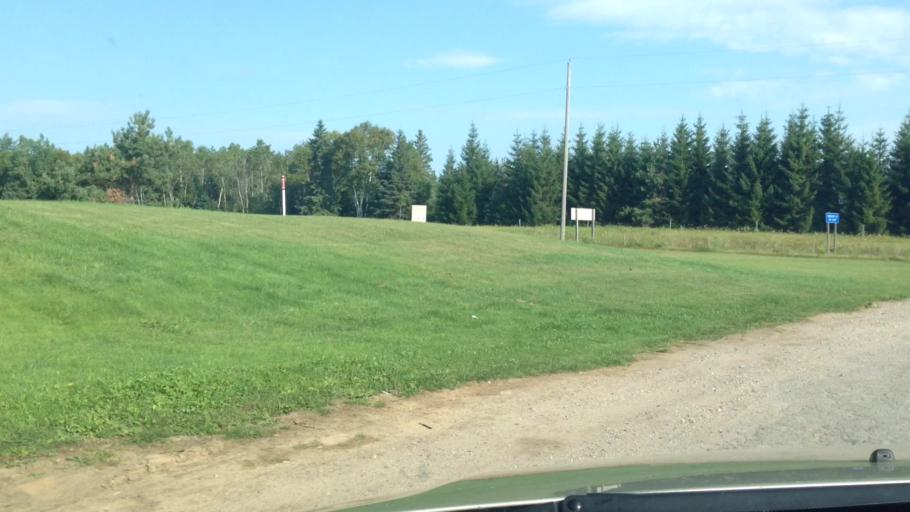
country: US
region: Michigan
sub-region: Schoolcraft County
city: Manistique
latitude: 46.1001
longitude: -85.9302
